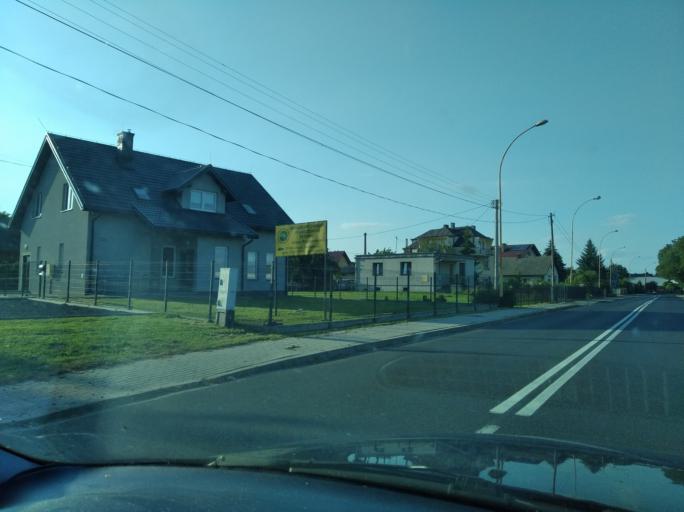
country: PL
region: Subcarpathian Voivodeship
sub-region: Powiat lezajski
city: Lezajsk
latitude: 50.2724
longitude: 22.4254
